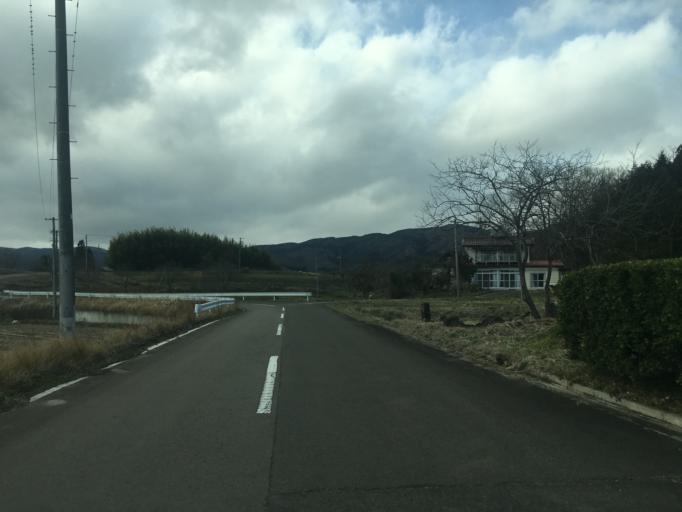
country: JP
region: Fukushima
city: Yanagawamachi-saiwaicho
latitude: 37.8864
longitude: 140.5957
